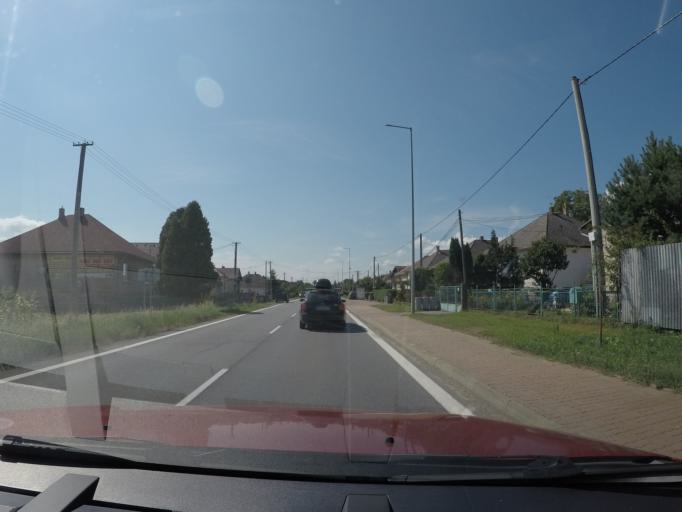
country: SK
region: Presovsky
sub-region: Okres Presov
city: Presov
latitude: 48.9321
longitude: 21.2408
